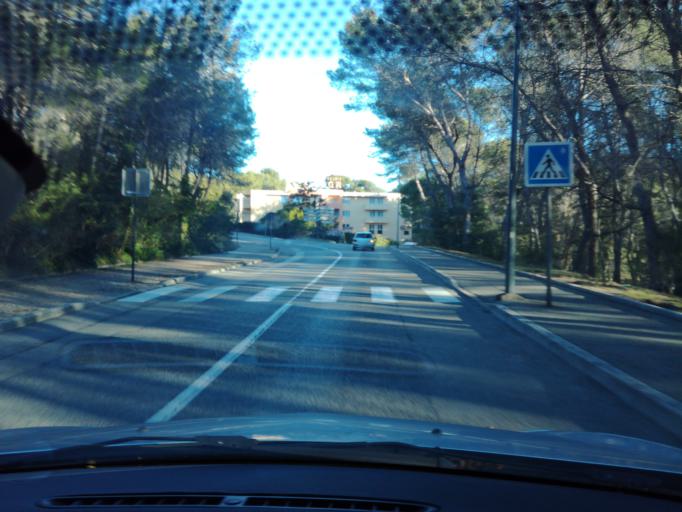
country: FR
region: Provence-Alpes-Cote d'Azur
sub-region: Departement des Alpes-Maritimes
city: Vallauris
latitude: 43.6133
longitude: 7.0538
